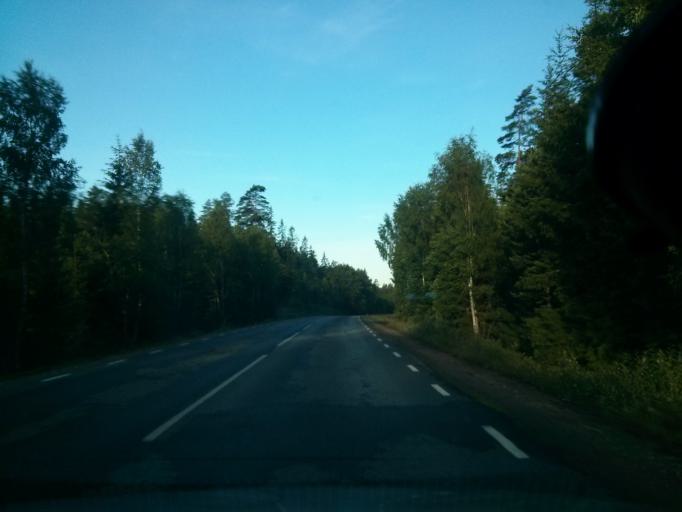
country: SE
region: Kronoberg
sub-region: Tingsryds Kommun
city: Tingsryd
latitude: 56.5395
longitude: 15.0097
